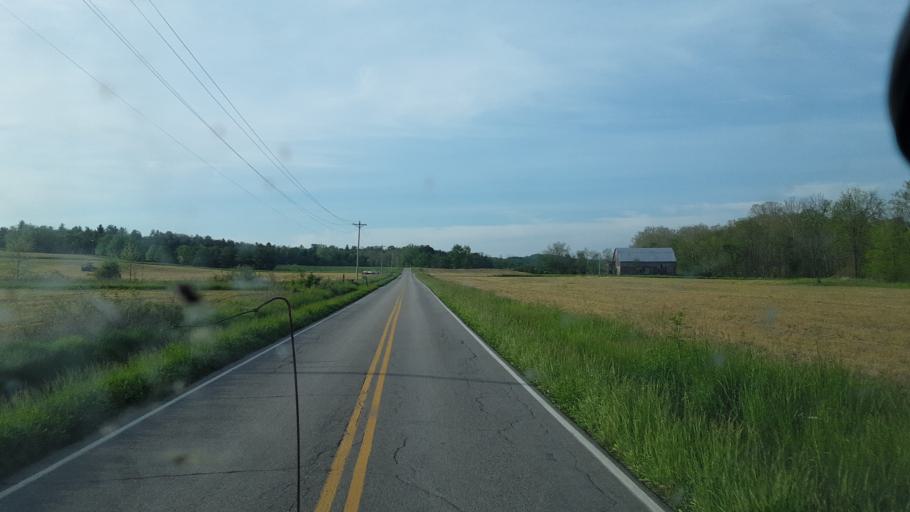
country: US
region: Ohio
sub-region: Ross County
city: Kingston
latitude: 39.5034
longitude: -82.6996
